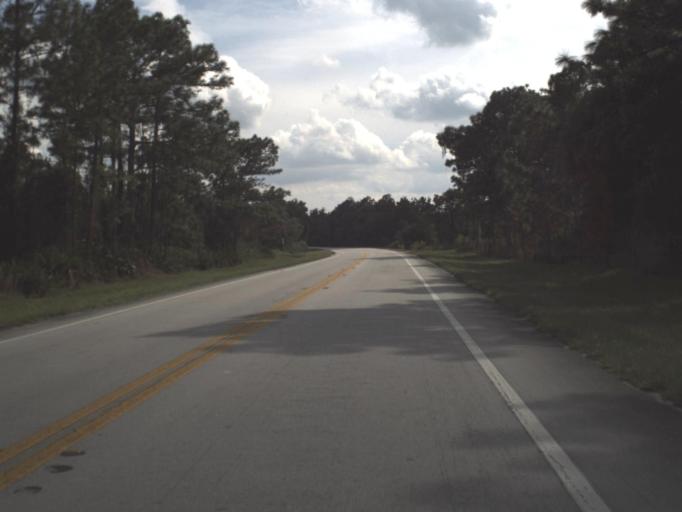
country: US
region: Florida
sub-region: Indian River County
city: Fellsmere
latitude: 27.5754
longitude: -80.8337
